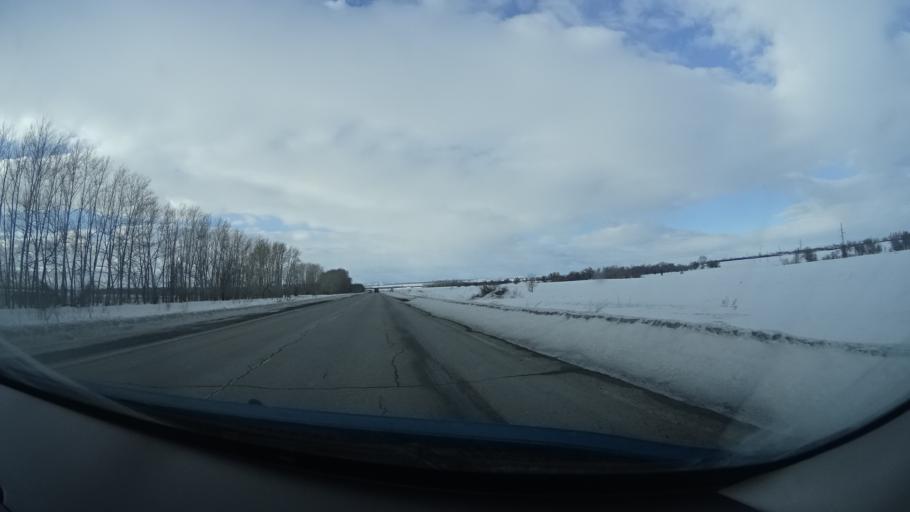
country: RU
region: Chelyabinsk
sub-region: Gorod Magnitogorsk
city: Magnitogorsk
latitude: 53.5756
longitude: 58.8914
